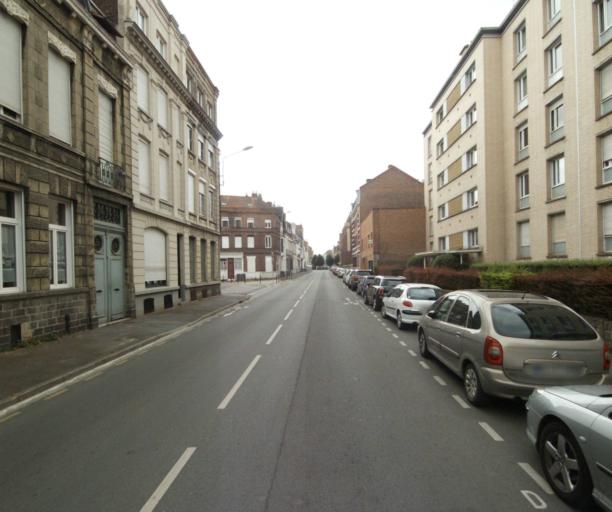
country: FR
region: Nord-Pas-de-Calais
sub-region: Departement du Nord
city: Armentieres
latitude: 50.6849
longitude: 2.8780
